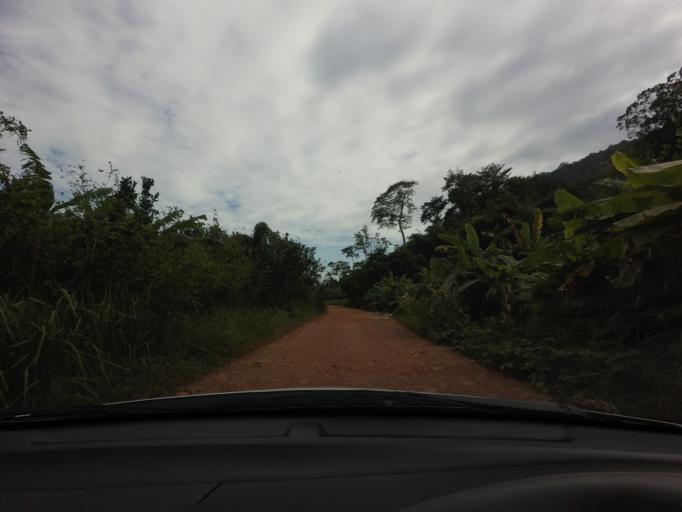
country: TH
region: Nakhon Nayok
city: Nakhon Nayok
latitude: 14.3467
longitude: 101.2756
